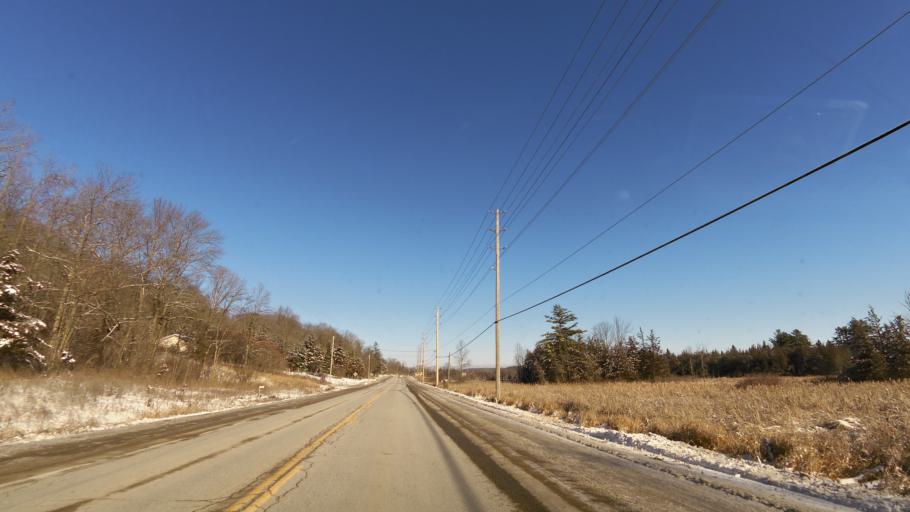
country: CA
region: Ontario
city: Quinte West
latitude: 44.2652
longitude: -77.8146
